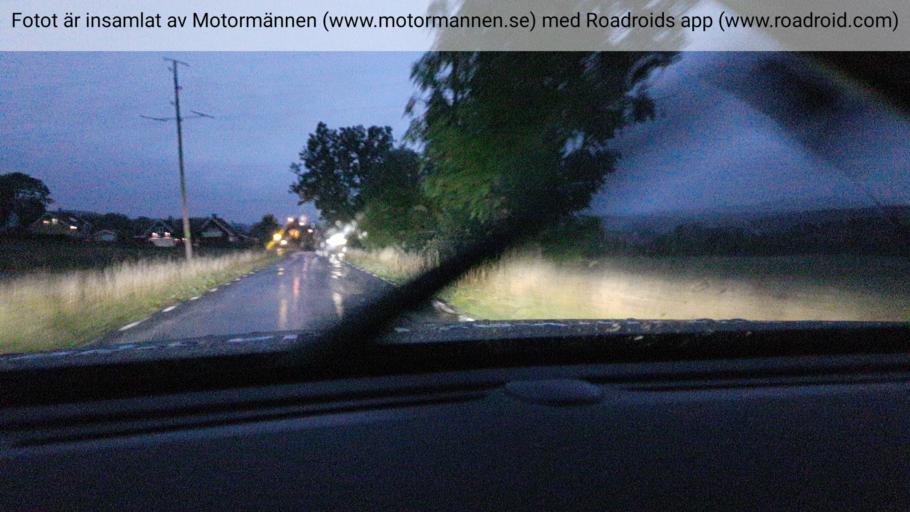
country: SE
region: Vaestra Goetaland
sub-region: Skovde Kommun
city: Skultorp
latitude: 58.2233
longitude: 13.8166
